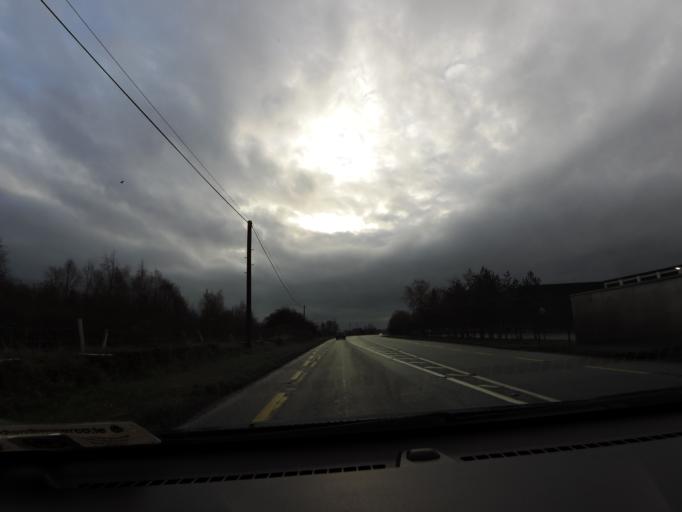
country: IE
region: Leinster
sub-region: Kilkenny
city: Ballyragget
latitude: 52.8001
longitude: -7.3503
